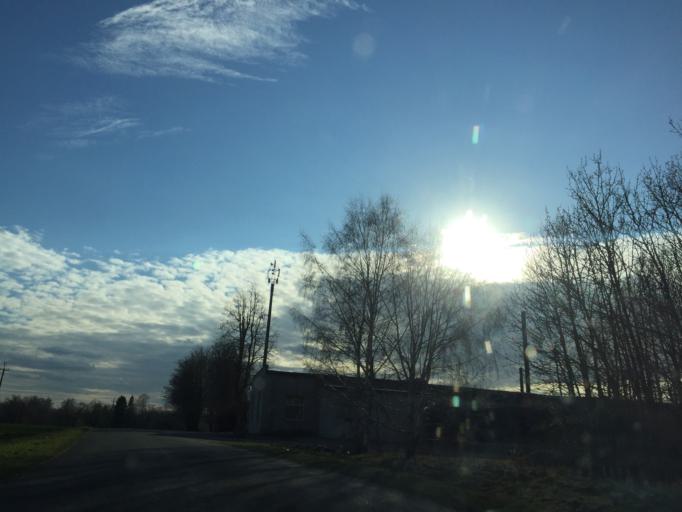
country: EE
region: Valgamaa
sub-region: Torva linn
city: Torva
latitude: 58.2138
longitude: 25.9375
